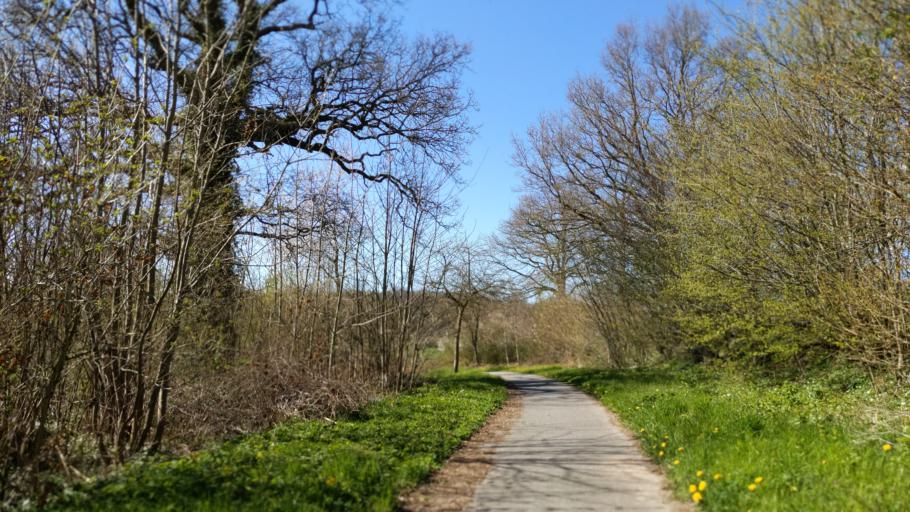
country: DE
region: Schleswig-Holstein
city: Susel
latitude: 54.1115
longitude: 10.6972
